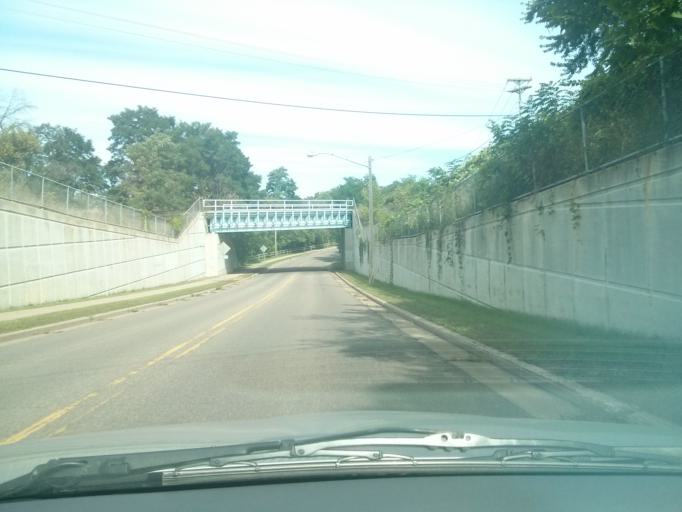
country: US
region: Wisconsin
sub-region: Saint Croix County
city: Hudson
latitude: 44.9826
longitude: -92.7434
